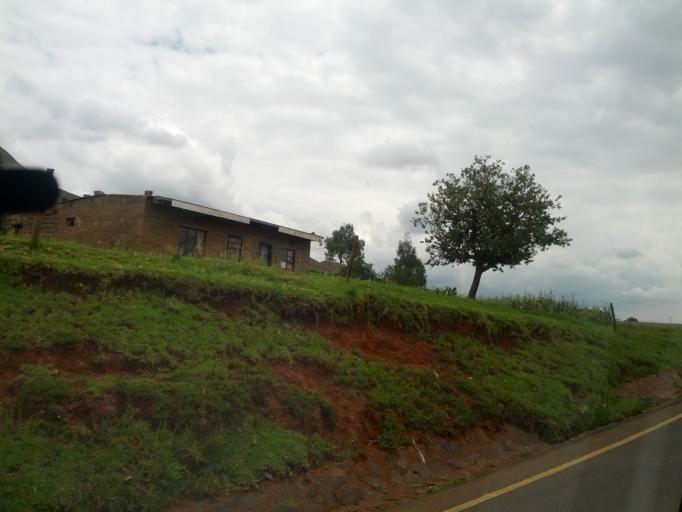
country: LS
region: Butha-Buthe
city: Butha-Buthe
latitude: -29.0336
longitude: 28.2753
